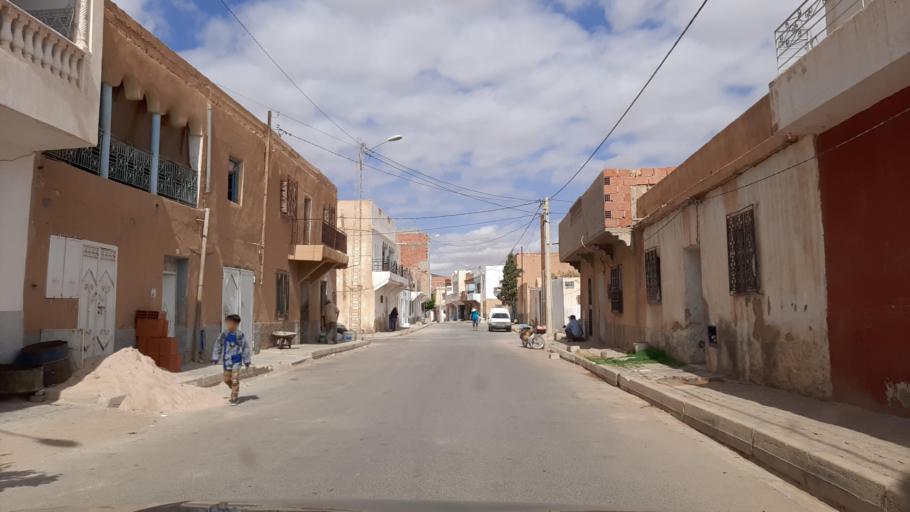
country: TN
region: Tataouine
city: Tataouine
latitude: 32.9295
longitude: 10.4551
